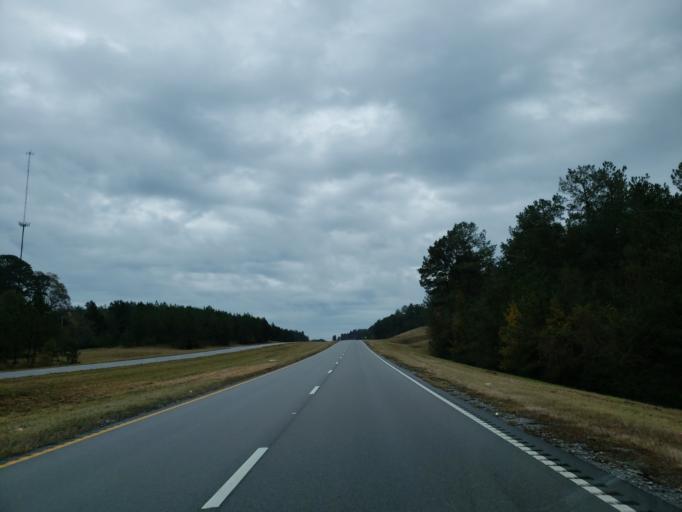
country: US
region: Mississippi
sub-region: Wayne County
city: Waynesboro
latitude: 31.6879
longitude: -88.7054
